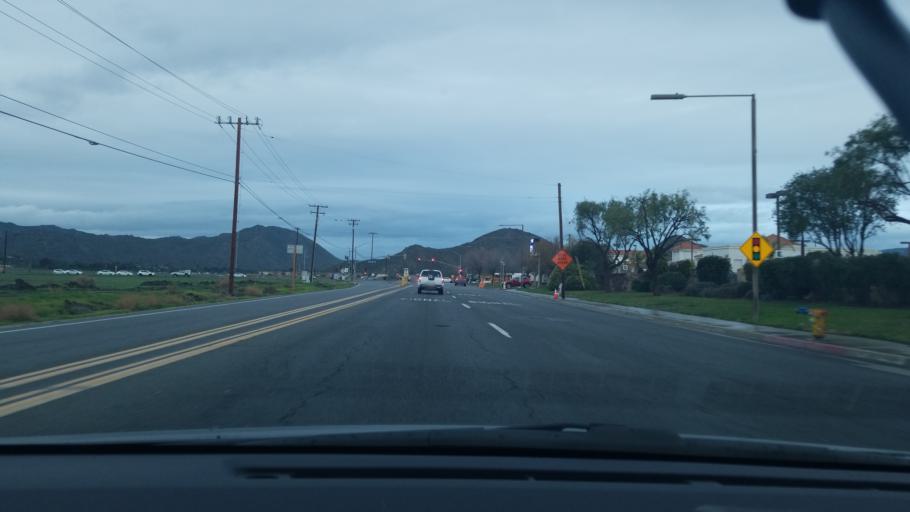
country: US
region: California
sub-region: Riverside County
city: Green Acres
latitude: 33.7420
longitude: -117.0328
